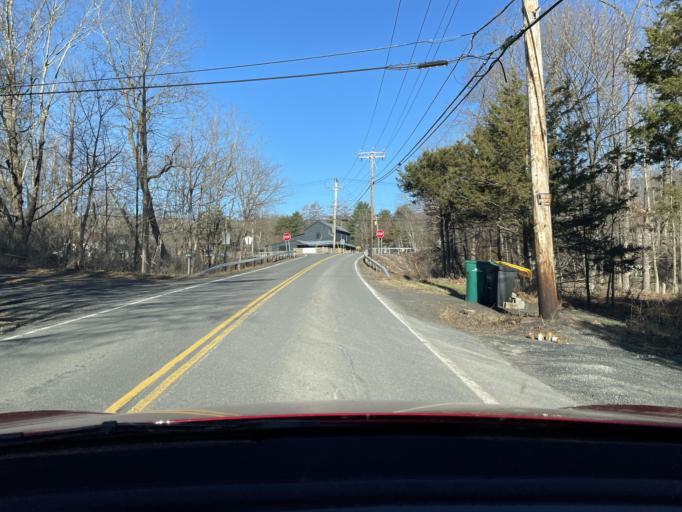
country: US
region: New York
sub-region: Ulster County
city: Zena
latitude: 42.0501
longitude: -74.0675
